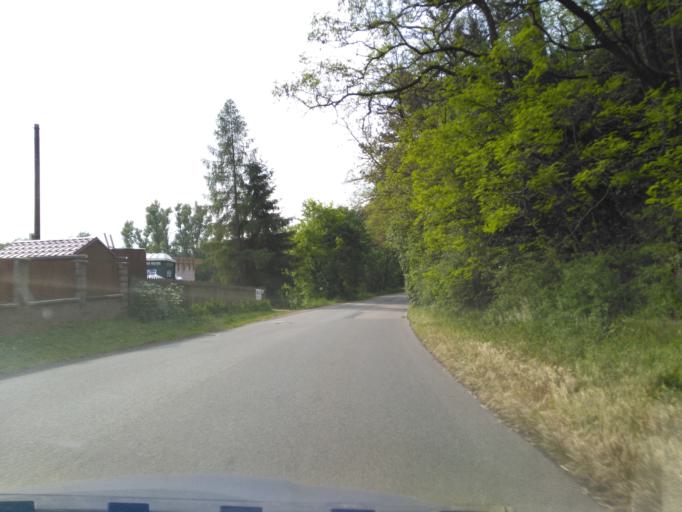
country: CZ
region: Central Bohemia
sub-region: Okres Beroun
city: Kraluv Dvur
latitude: 49.9549
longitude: 14.0139
